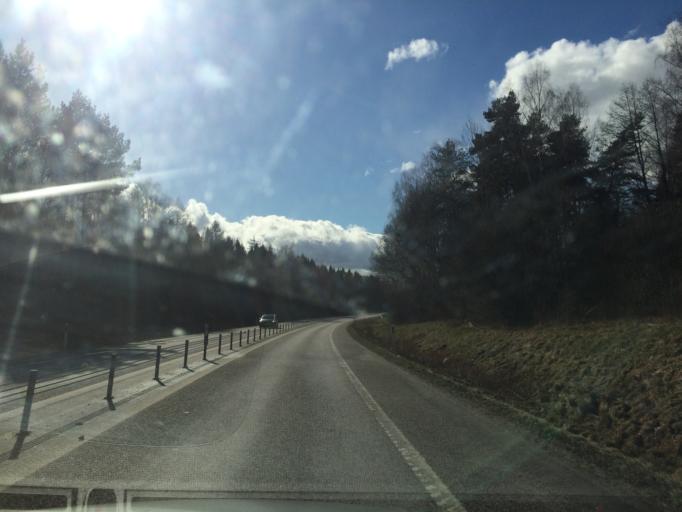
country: SE
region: Vaestra Goetaland
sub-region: Skara Kommun
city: Skara
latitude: 58.3813
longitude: 13.4571
